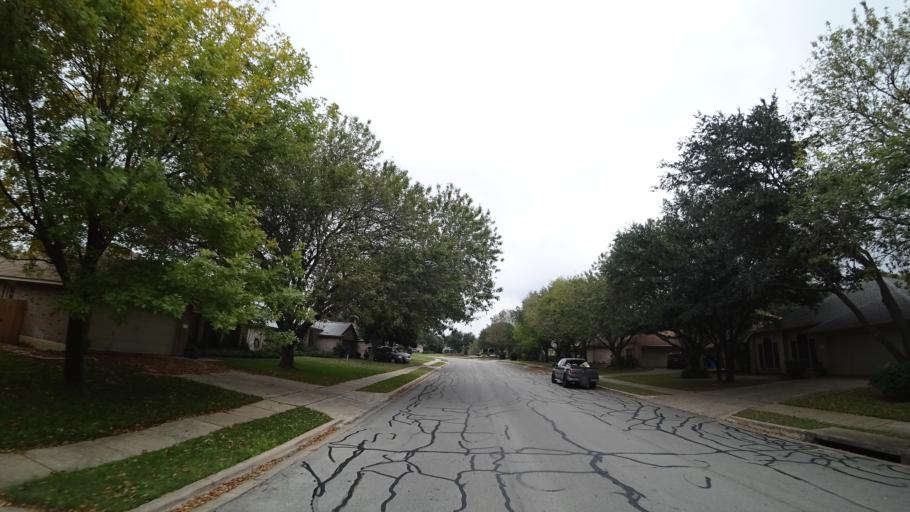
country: US
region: Texas
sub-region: Travis County
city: Pflugerville
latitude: 30.4489
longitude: -97.6120
